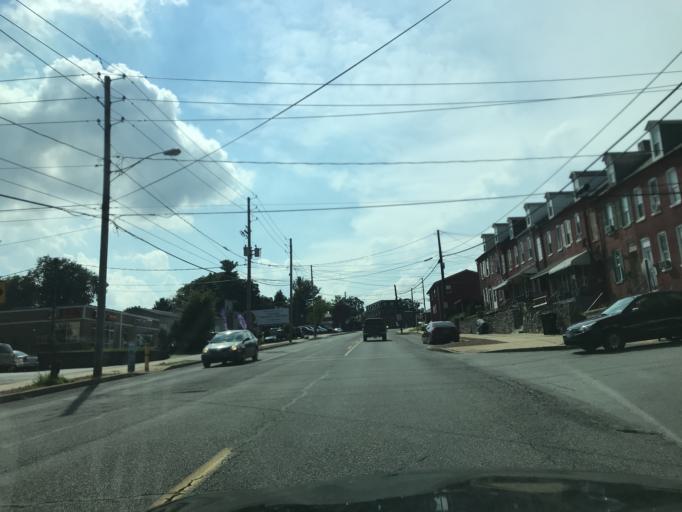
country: US
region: Pennsylvania
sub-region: Lancaster County
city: Columbia
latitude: 40.0319
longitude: -76.4913
